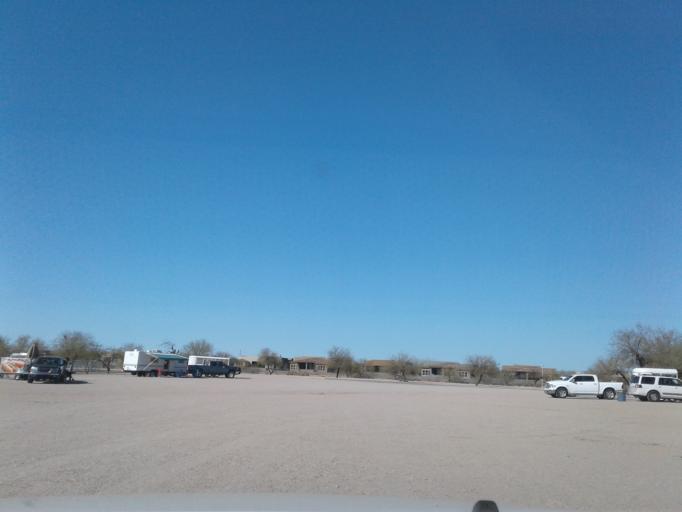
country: US
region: Arizona
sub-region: Maricopa County
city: Paradise Valley
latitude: 33.6628
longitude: -111.9858
